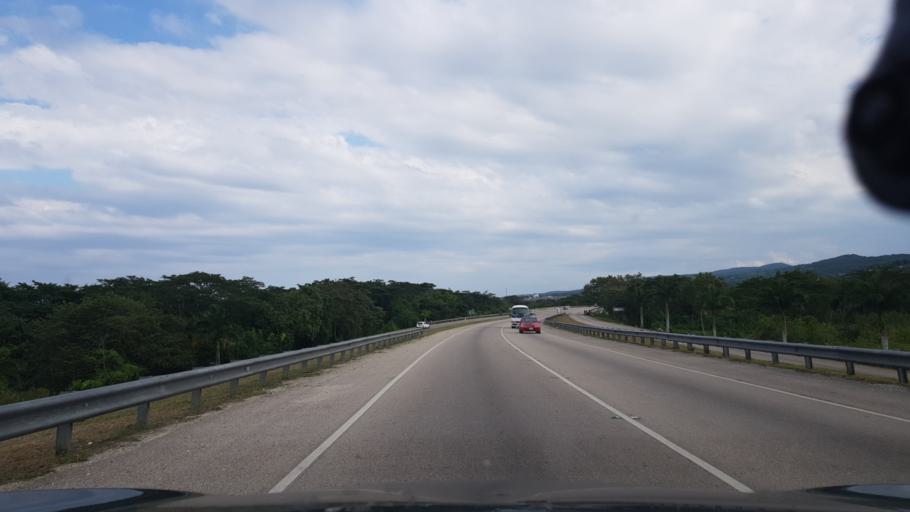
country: JM
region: Trelawny
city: Falmouth
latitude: 18.4766
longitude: -77.6587
